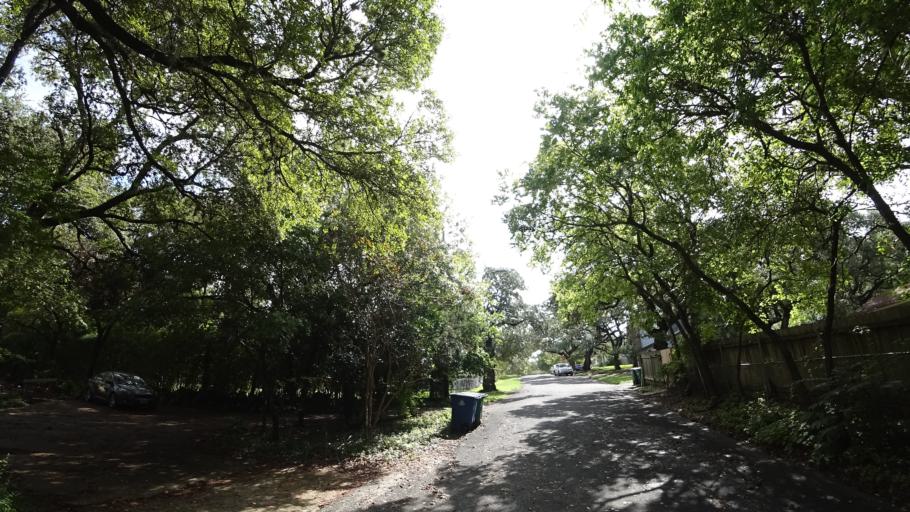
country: US
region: Texas
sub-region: Travis County
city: West Lake Hills
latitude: 30.3473
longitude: -97.7437
